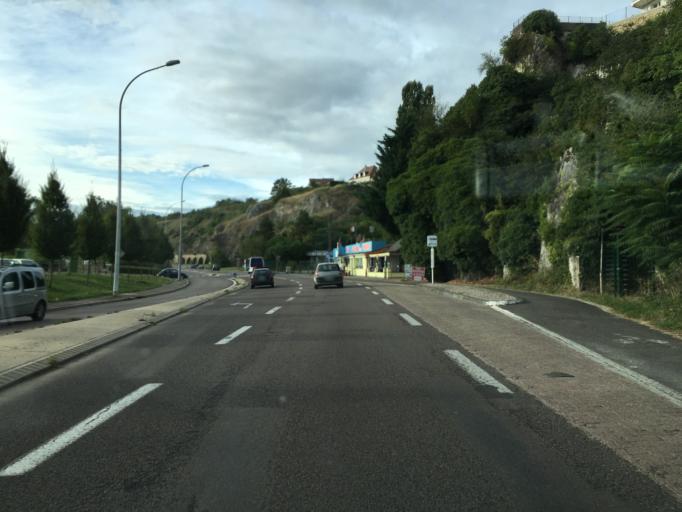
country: FR
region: Bourgogne
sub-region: Departement de la Cote-d'Or
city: Dijon
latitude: 47.3245
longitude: 5.0087
